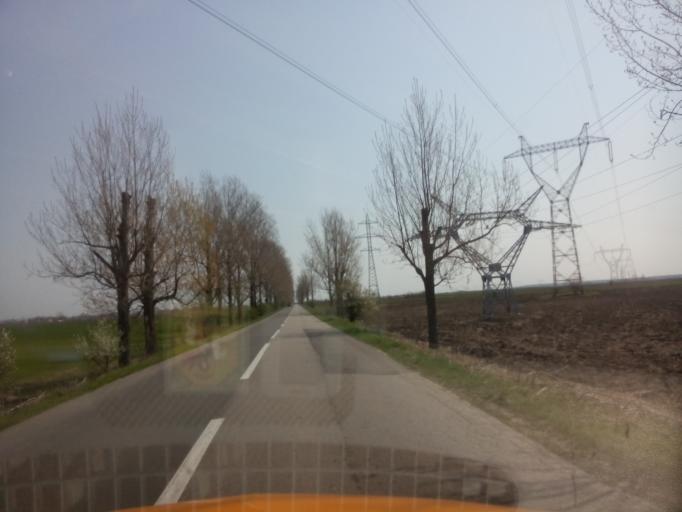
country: RO
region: Calarasi
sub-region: Comuna Luica
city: Luica
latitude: 44.2251
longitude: 26.5653
